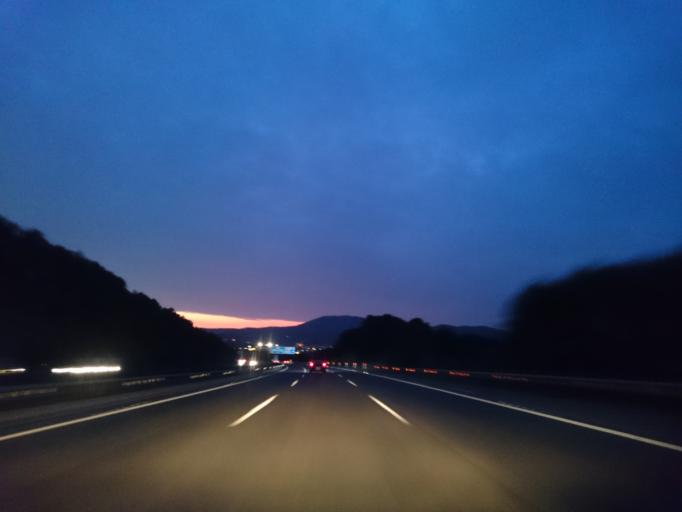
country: ES
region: Catalonia
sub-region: Provincia de Barcelona
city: Sitges
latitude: 41.2524
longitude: 1.7977
